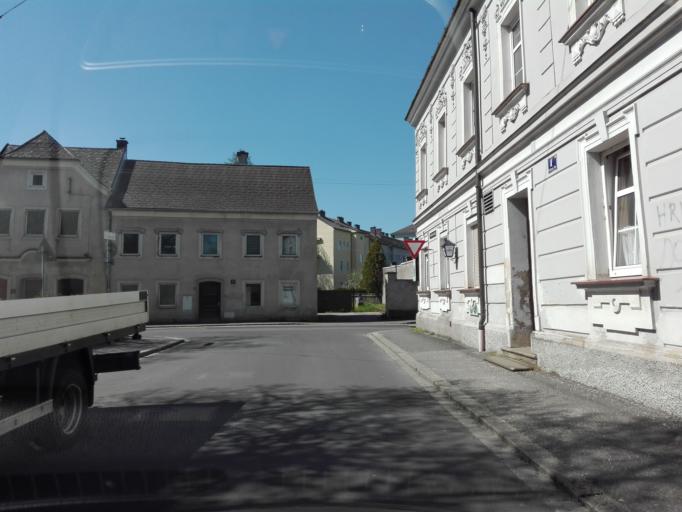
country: AT
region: Upper Austria
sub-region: Politischer Bezirk Linz-Land
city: Ansfelden
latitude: 48.2542
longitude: 14.3137
